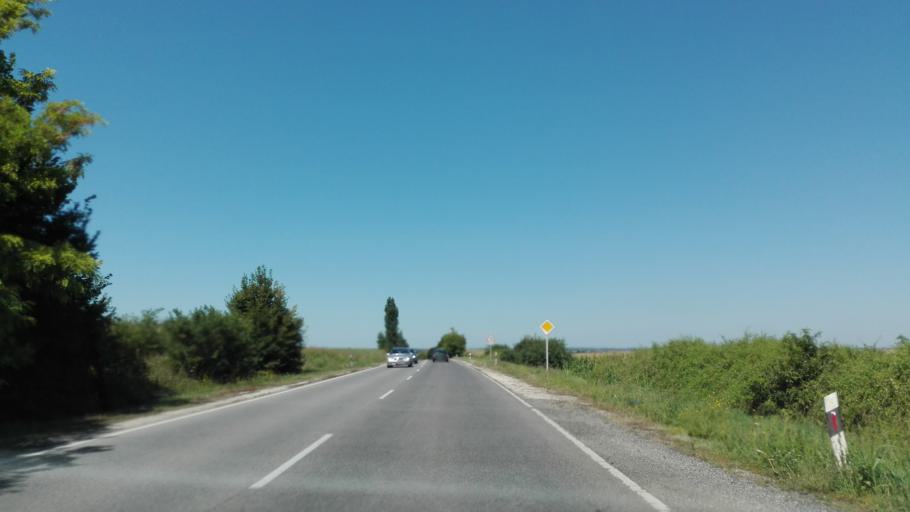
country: HU
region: Fejer
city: Mezoszilas
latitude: 46.8328
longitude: 18.4537
